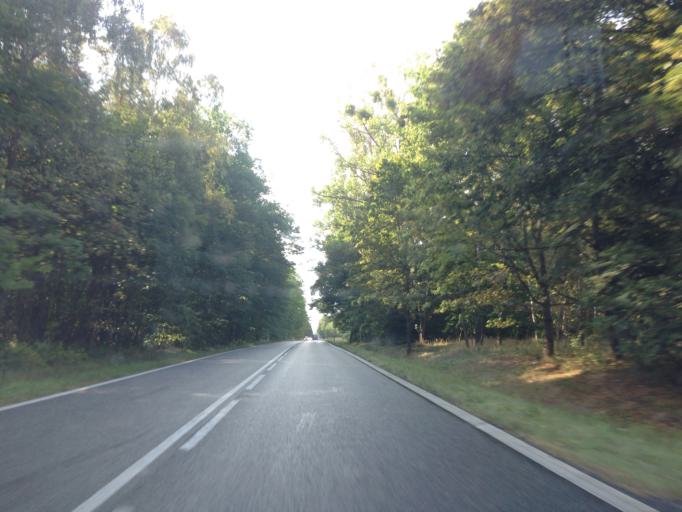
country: PL
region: Kujawsko-Pomorskie
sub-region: Powiat swiecki
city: Lniano
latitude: 53.4660
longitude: 18.1743
